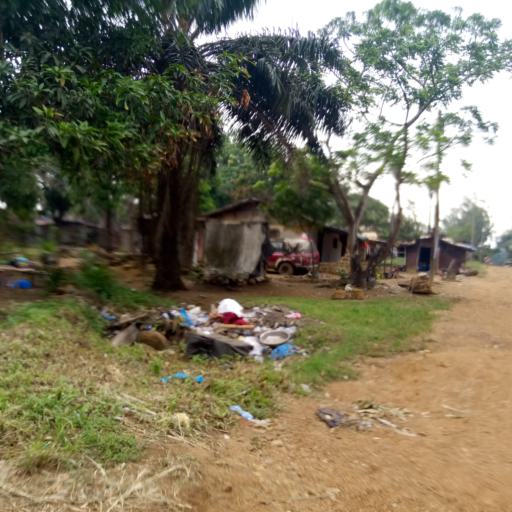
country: LR
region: Montserrado
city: Monrovia
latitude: 6.3014
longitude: -10.6874
